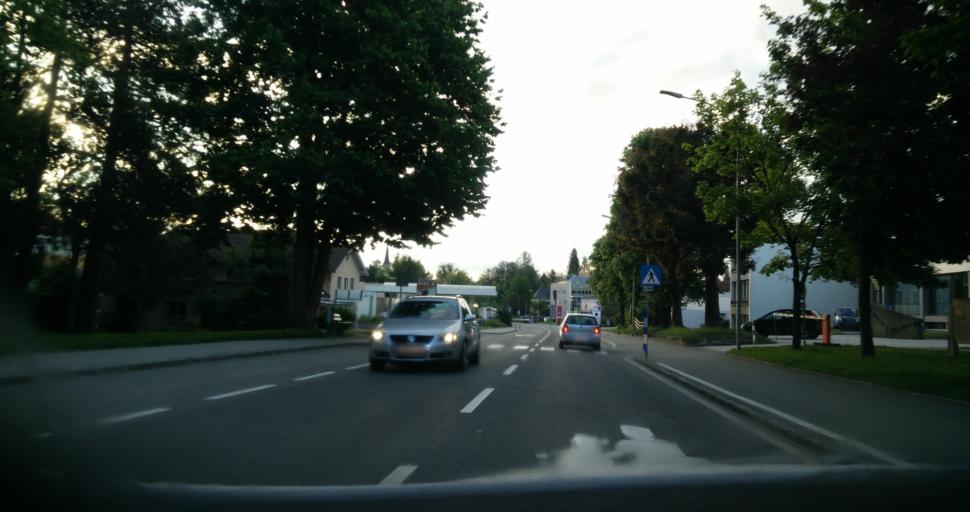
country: AT
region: Carinthia
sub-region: Villach Stadt
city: Villach
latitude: 46.6136
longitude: 13.8333
